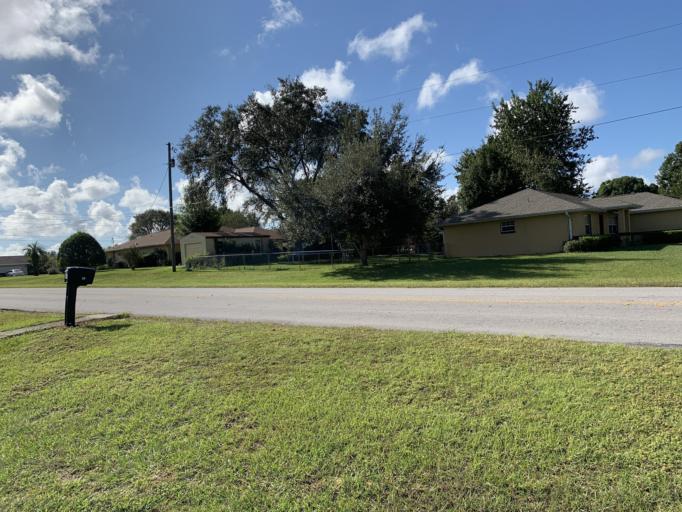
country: US
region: Florida
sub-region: Marion County
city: Silver Springs Shores
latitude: 29.1579
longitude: -82.0475
